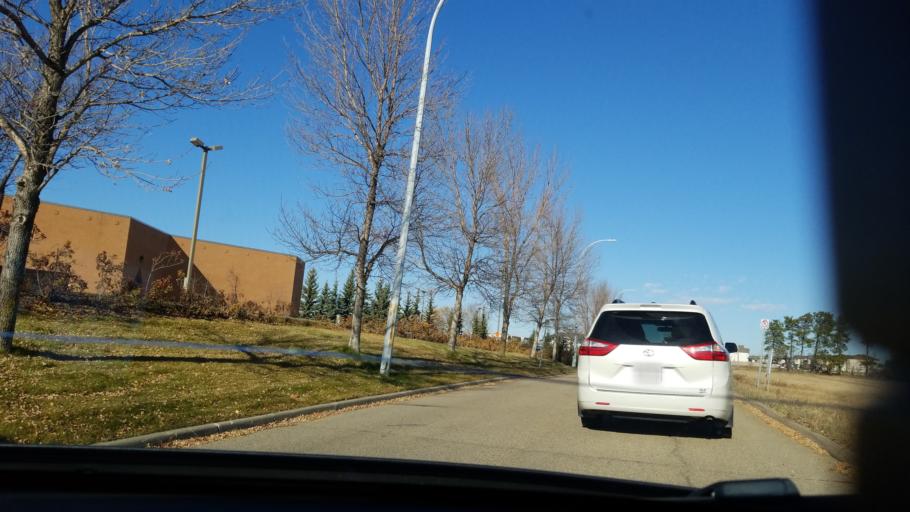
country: CA
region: Alberta
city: Edmonton
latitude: 53.6144
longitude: -113.4879
